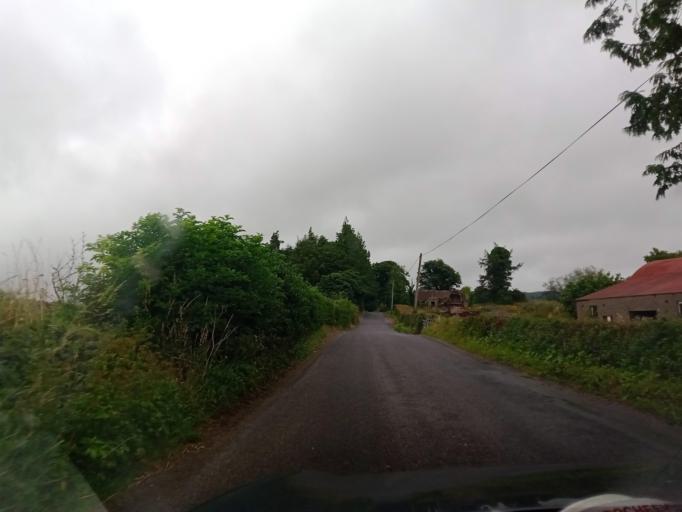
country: IE
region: Leinster
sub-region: Laois
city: Abbeyleix
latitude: 52.9244
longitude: -7.2816
